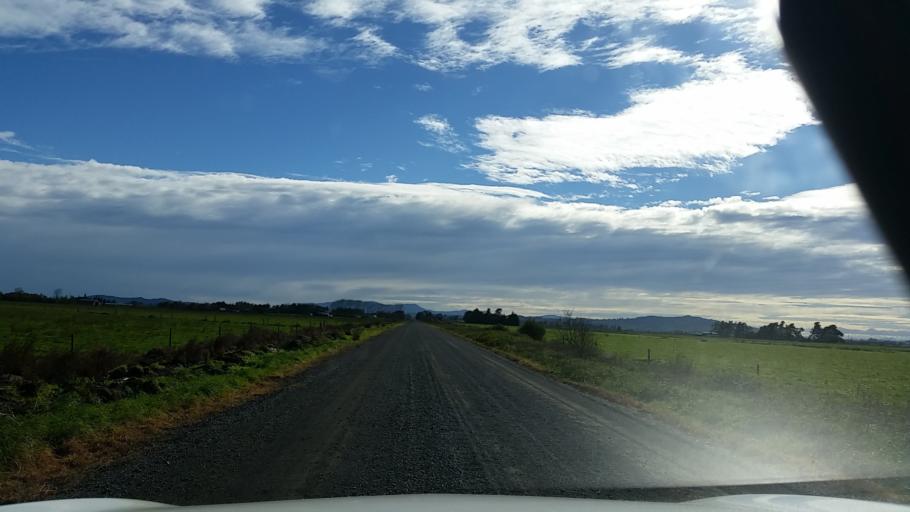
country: NZ
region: Waikato
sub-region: Hamilton City
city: Hamilton
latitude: -37.6773
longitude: 175.4423
